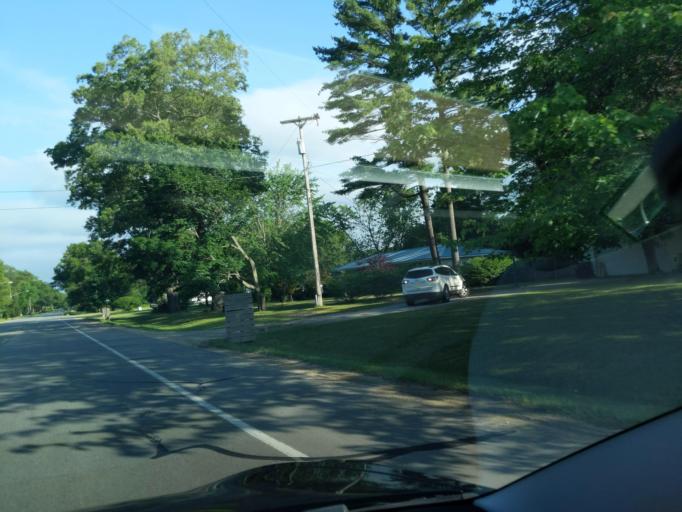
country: US
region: Michigan
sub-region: Muskegon County
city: Whitehall
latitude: 43.3984
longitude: -86.3058
